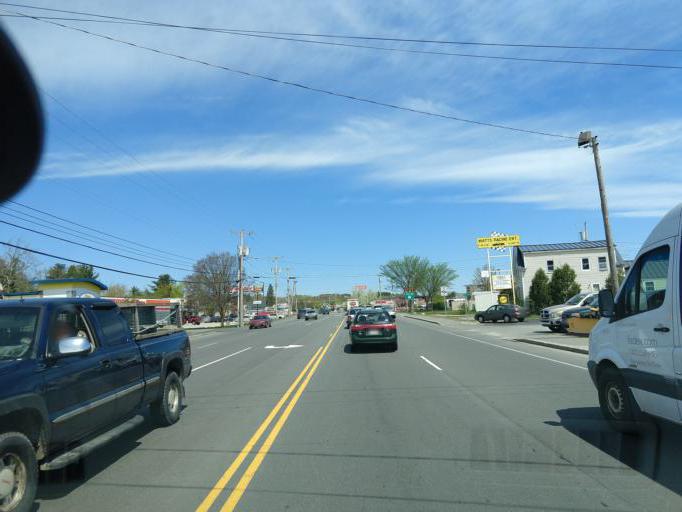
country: US
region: New Hampshire
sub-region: Rockingham County
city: Seabrook
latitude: 42.8892
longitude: -70.8716
